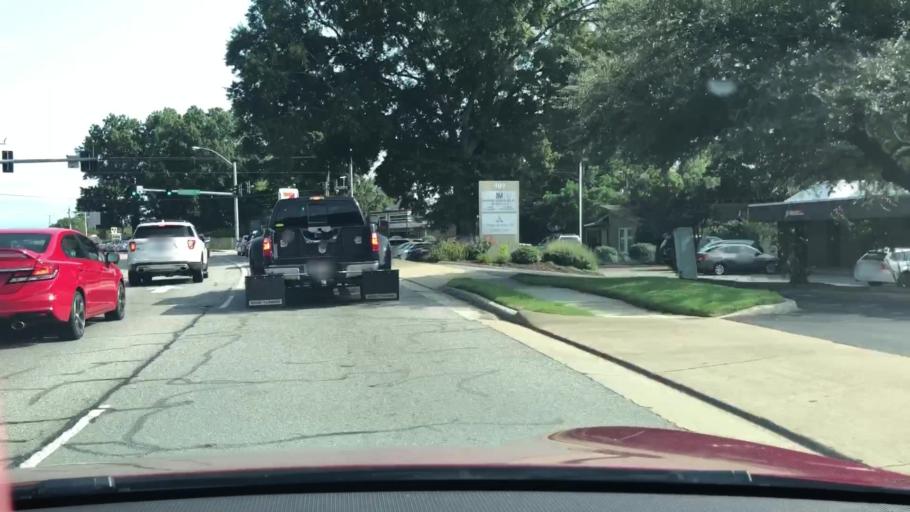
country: US
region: Virginia
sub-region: City of Virginia Beach
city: Virginia Beach
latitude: 36.8559
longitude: -76.0254
